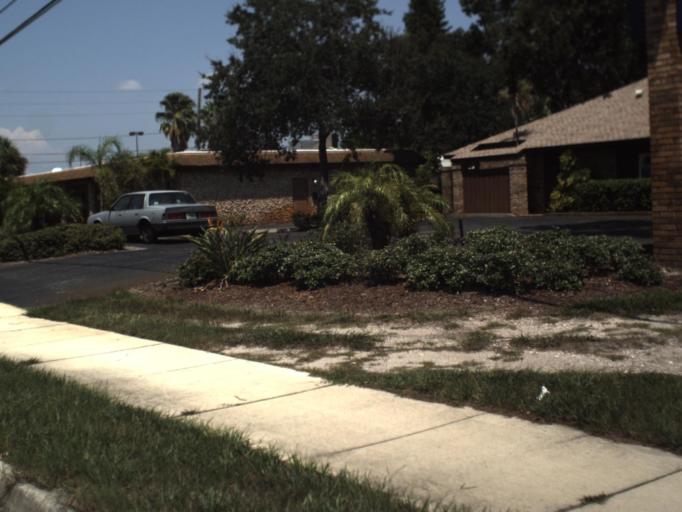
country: US
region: Florida
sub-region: Pinellas County
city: Kenneth City
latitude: 27.7866
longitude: -82.7283
